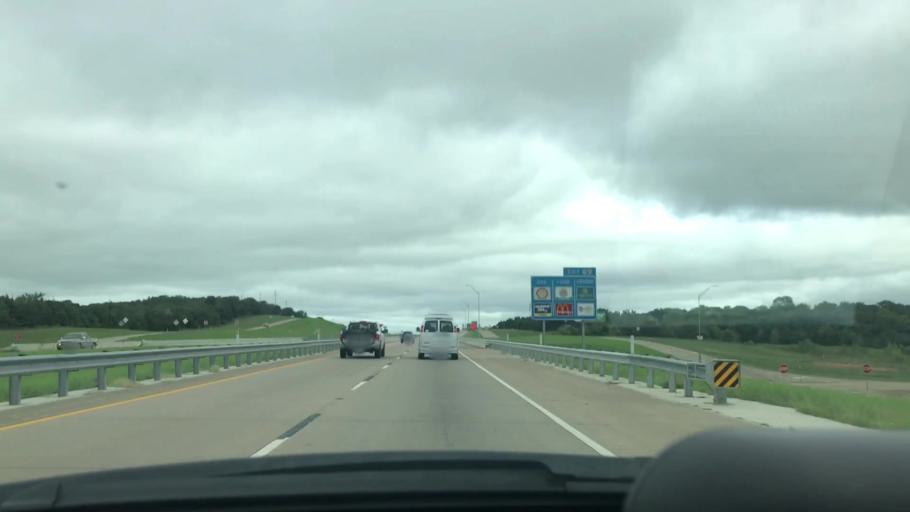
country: US
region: Texas
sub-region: Grayson County
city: Denison
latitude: 33.7473
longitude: -96.5842
